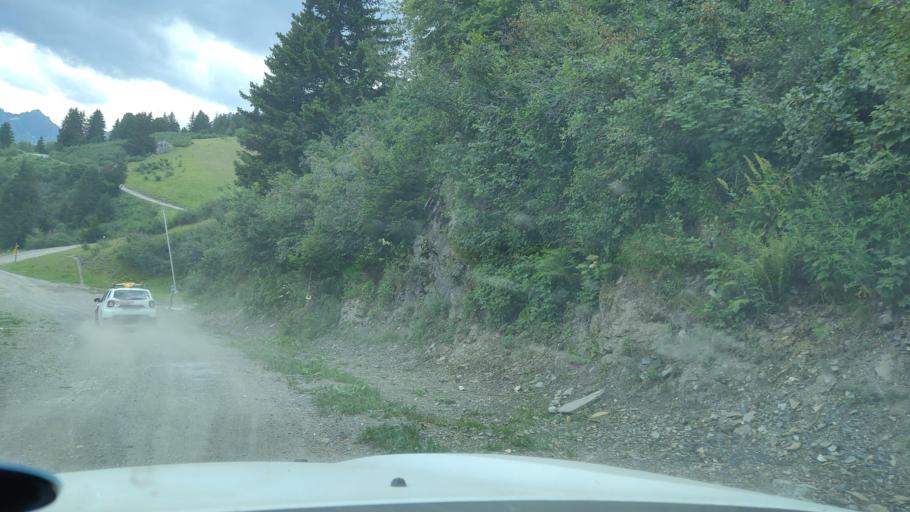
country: FR
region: Rhone-Alpes
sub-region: Departement de la Savoie
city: Meribel
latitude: 45.3744
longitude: 6.5674
